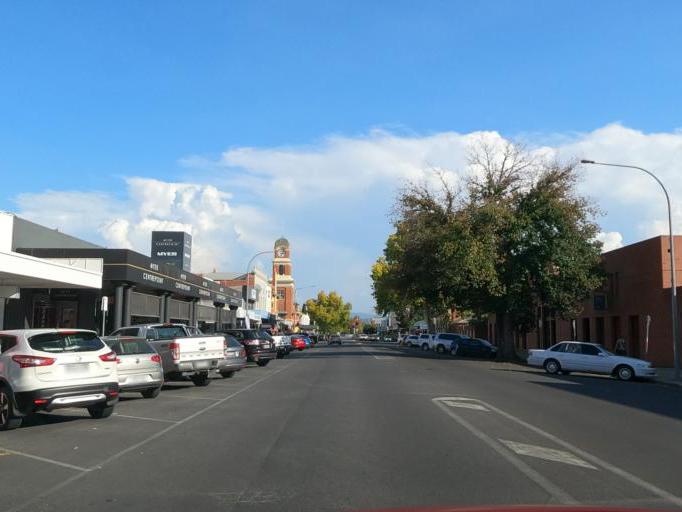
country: AU
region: New South Wales
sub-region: Albury Municipality
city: Albury
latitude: -36.0798
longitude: 146.9184
